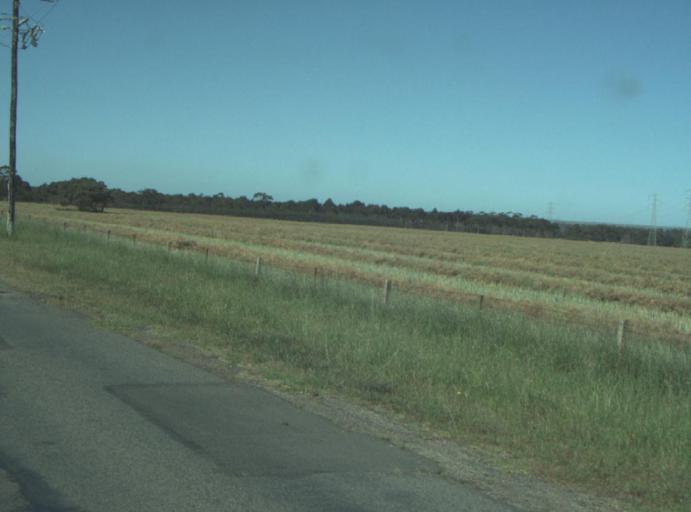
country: AU
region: Victoria
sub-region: Greater Geelong
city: Lara
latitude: -37.9327
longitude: 144.3942
